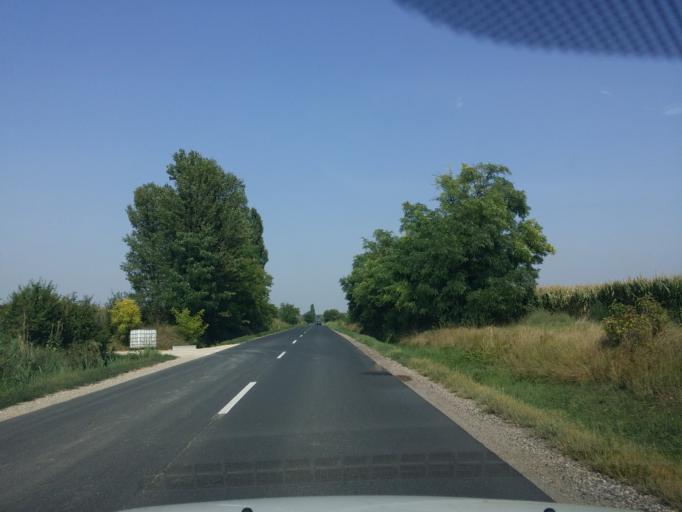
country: HU
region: Fejer
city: Sarbogard
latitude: 46.8987
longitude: 18.6398
